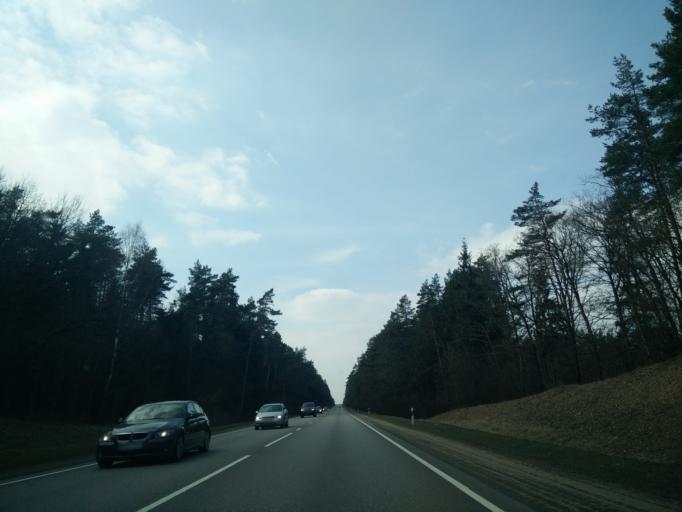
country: LT
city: Lentvaris
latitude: 54.6237
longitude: 25.0204
